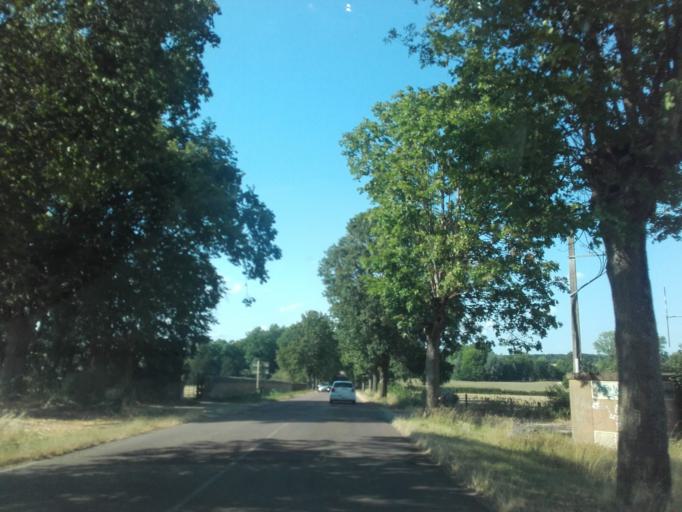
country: FR
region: Bourgogne
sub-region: Departement de Saone-et-Loire
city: Dracy-le-Fort
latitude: 46.8022
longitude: 4.7524
